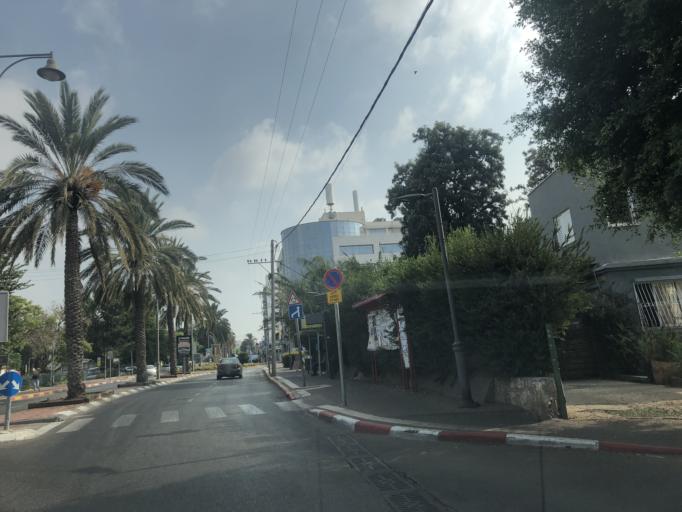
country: IL
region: Central District
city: Rosh Ha'Ayin
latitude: 32.0977
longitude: 34.9426
